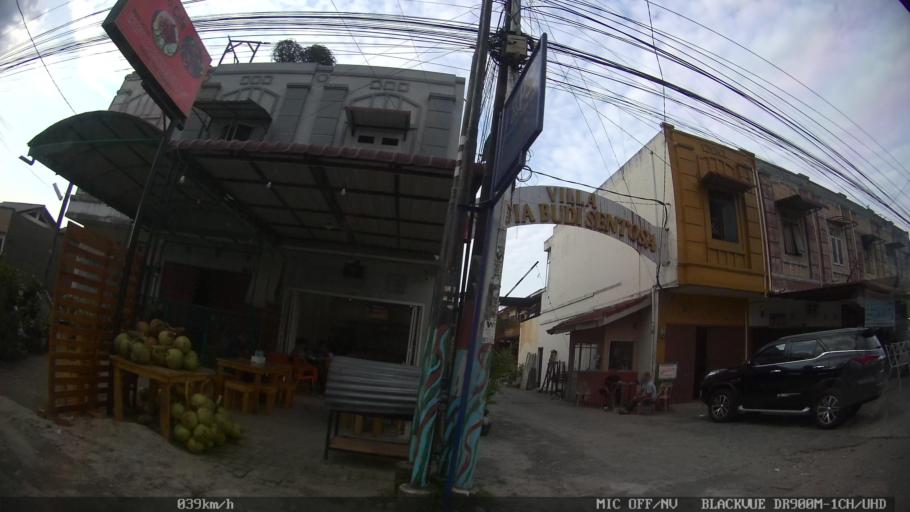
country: ID
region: North Sumatra
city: Sunggal
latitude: 3.5550
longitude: 98.6297
